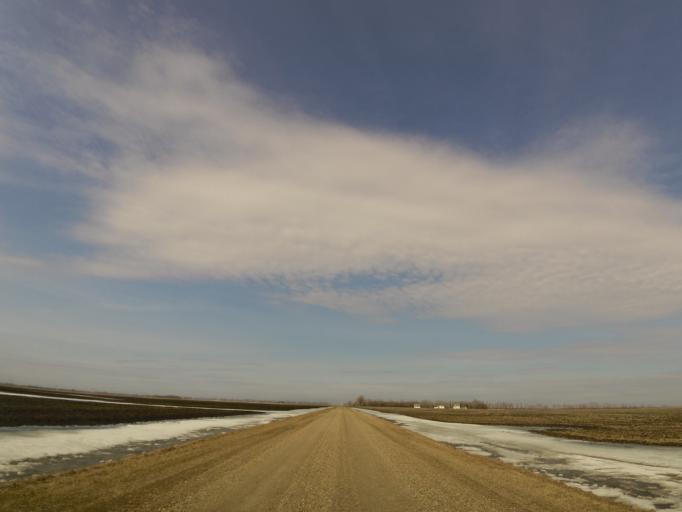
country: US
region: North Dakota
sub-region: Walsh County
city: Grafton
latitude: 48.4206
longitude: -97.2556
